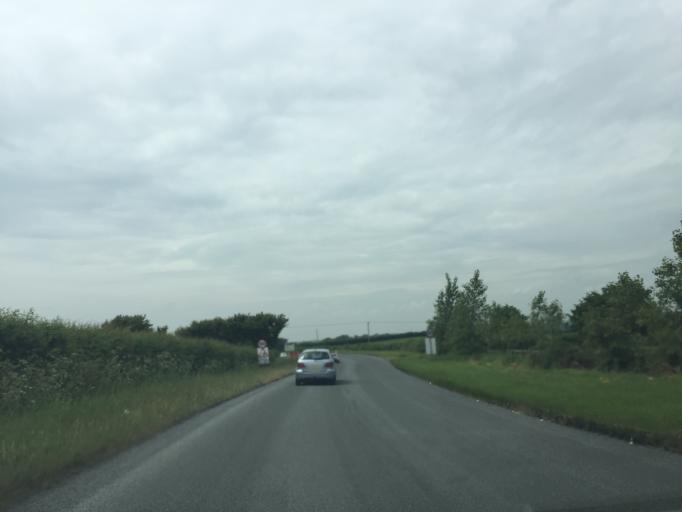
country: GB
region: England
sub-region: Dorset
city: Bovington Camp
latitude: 50.6640
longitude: -2.3187
